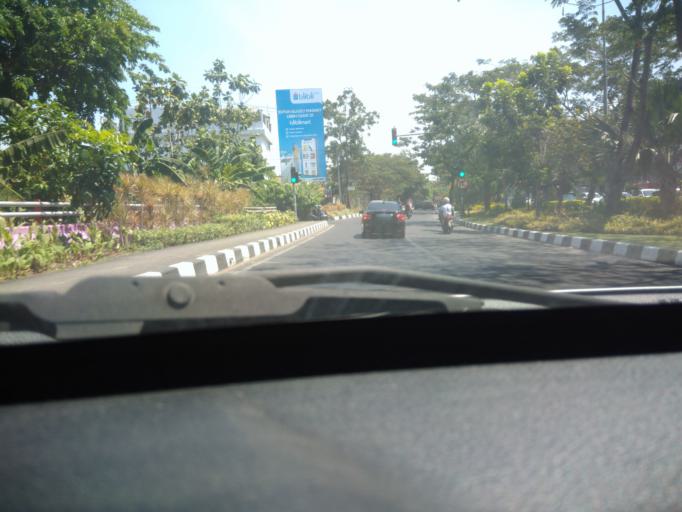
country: ID
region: East Java
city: Semampir
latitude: -7.3077
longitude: 112.7804
